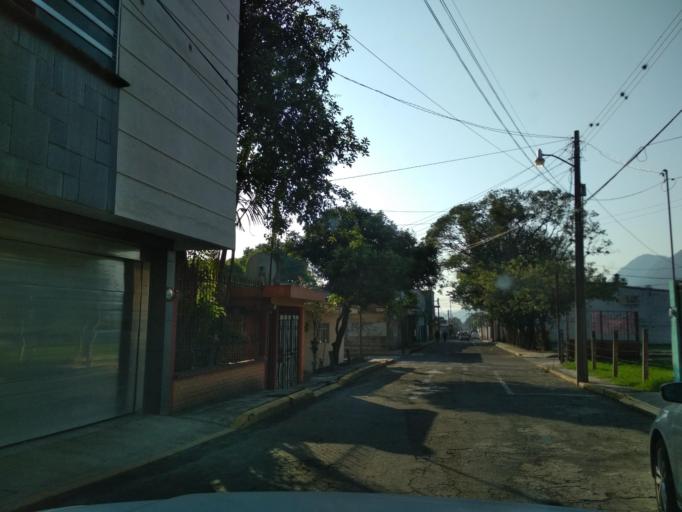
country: MX
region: Veracruz
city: Ixtac Zoquitlan
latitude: 18.8615
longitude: -97.0788
